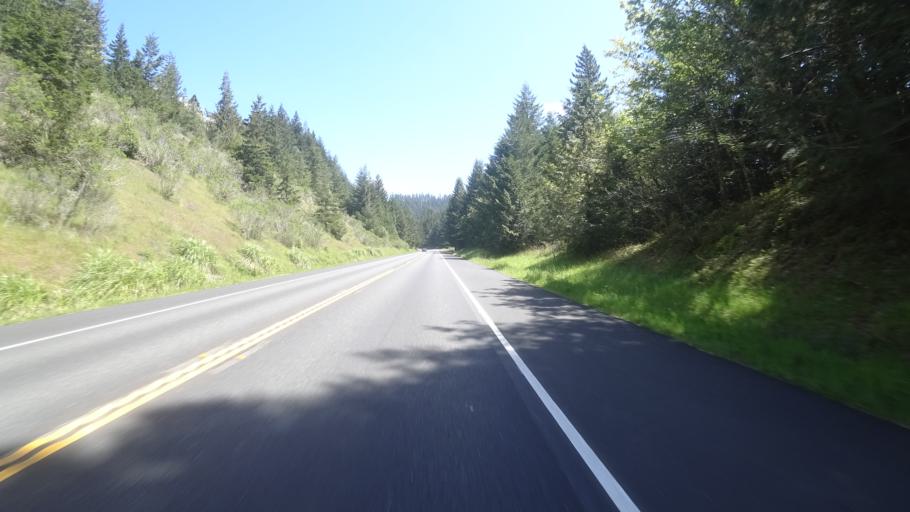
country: US
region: California
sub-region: Humboldt County
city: Blue Lake
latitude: 40.8994
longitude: -123.9225
